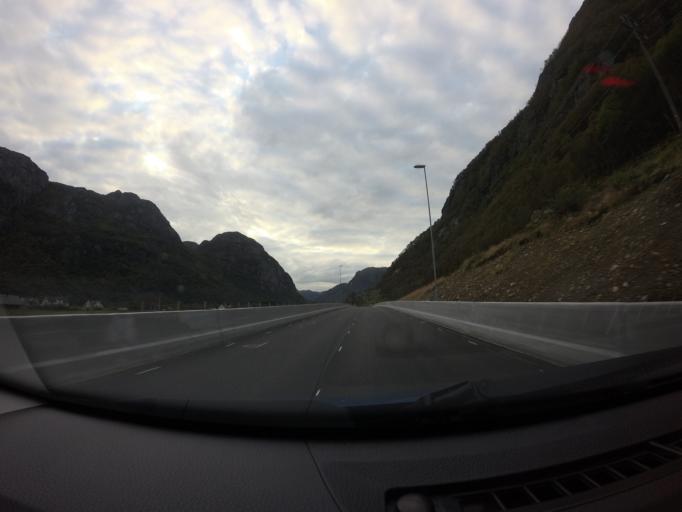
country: NO
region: Rogaland
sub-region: Forsand
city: Forsand
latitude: 58.8336
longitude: 6.1776
